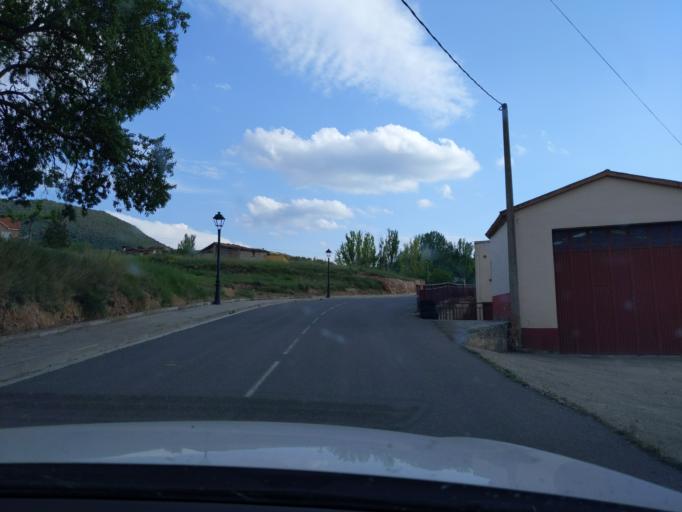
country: ES
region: La Rioja
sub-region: Provincia de La Rioja
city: Clavijo
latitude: 42.3679
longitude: -2.4233
